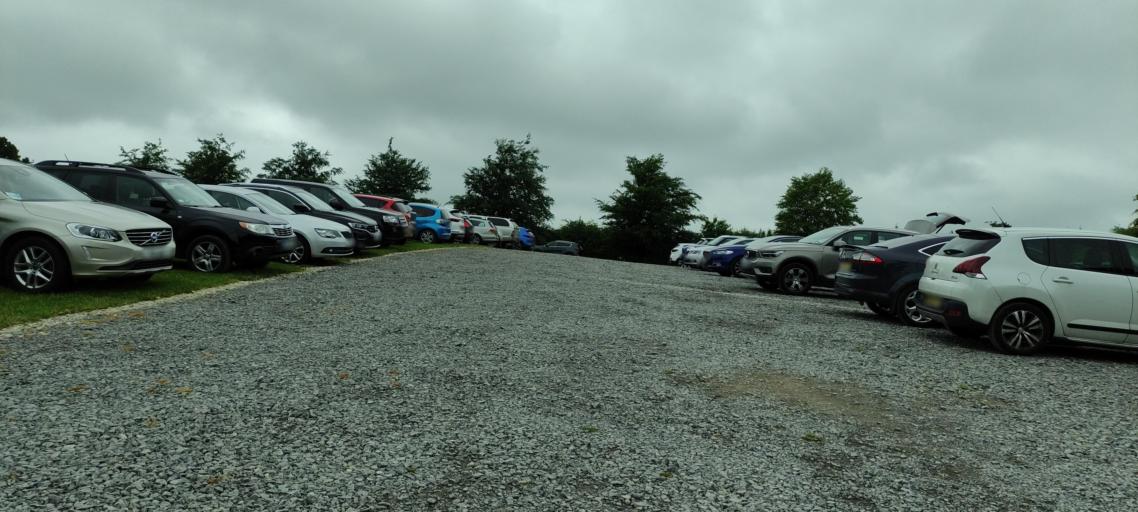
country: GB
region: England
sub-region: North Yorkshire
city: Bedale
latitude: 54.1923
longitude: -1.6776
